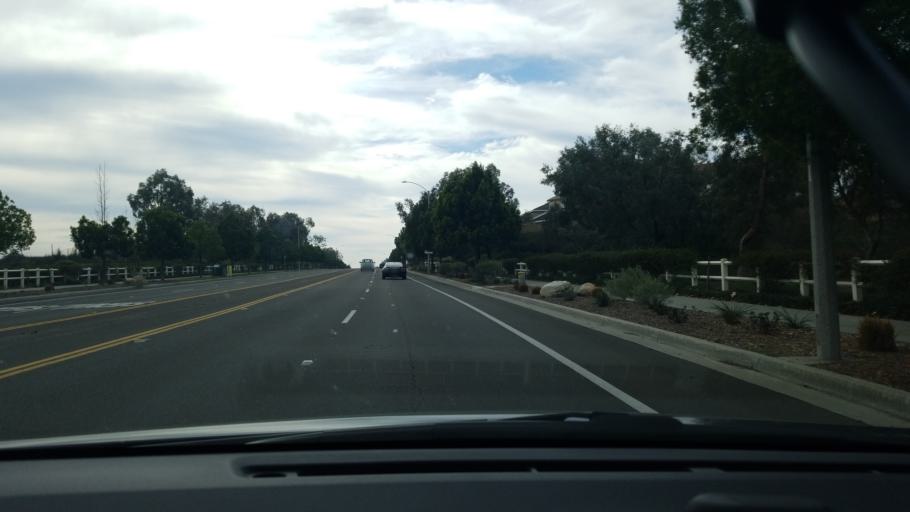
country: US
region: California
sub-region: Riverside County
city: Murrieta Hot Springs
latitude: 33.5603
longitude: -117.1100
